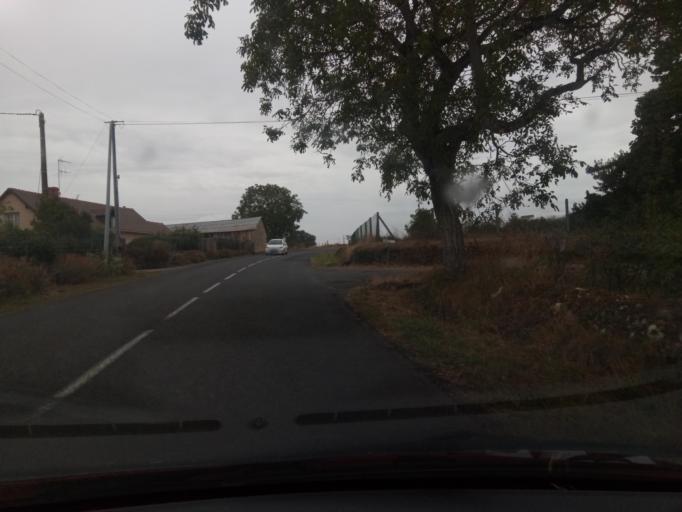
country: FR
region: Centre
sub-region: Departement de l'Indre
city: Tournon-Saint-Martin
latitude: 46.6883
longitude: 0.8778
